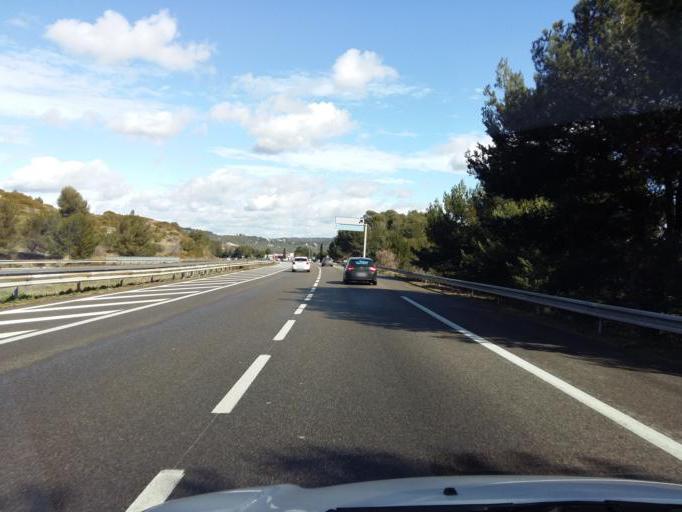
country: FR
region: Provence-Alpes-Cote d'Azur
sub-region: Departement des Bouches-du-Rhone
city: Cabries
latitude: 43.4304
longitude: 5.3920
